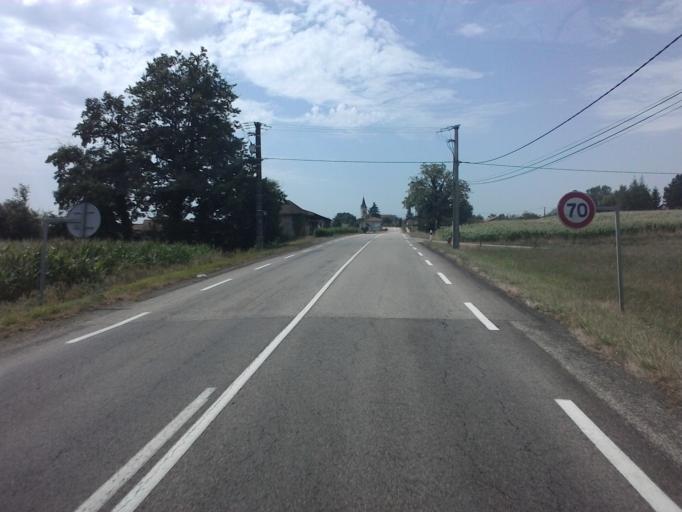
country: FR
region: Rhone-Alpes
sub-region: Departement de l'Ain
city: Coligny
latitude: 46.3501
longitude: 5.3240
